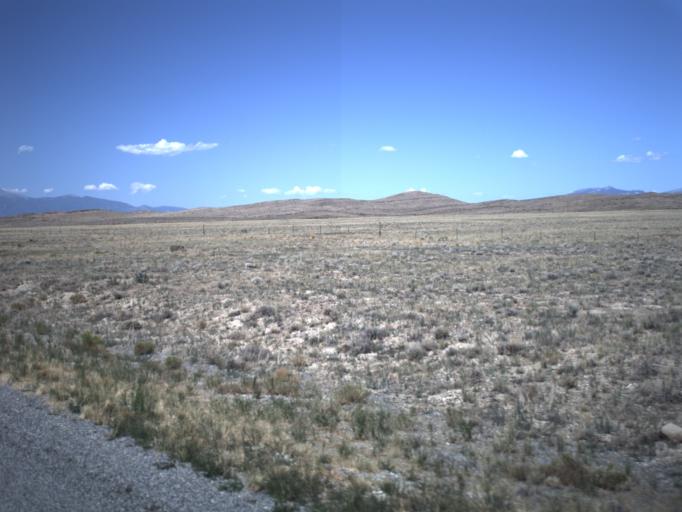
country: US
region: Utah
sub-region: Beaver County
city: Milford
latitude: 39.0471
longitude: -113.7938
